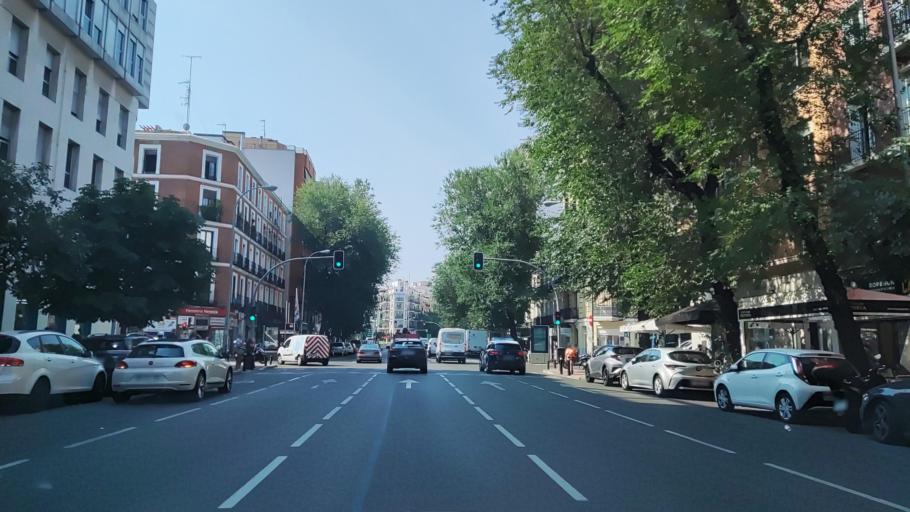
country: ES
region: Madrid
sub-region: Provincia de Madrid
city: Chamberi
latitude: 40.4353
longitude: -3.7043
